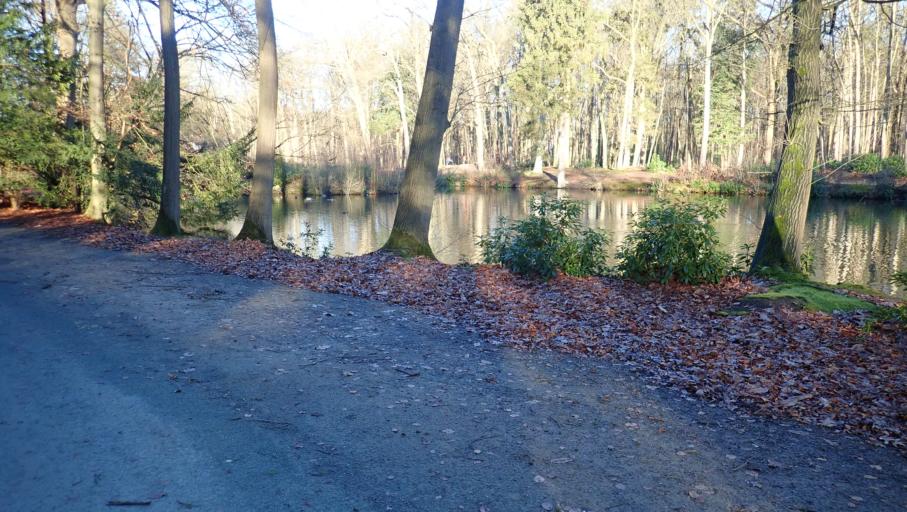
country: BE
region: Flanders
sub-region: Provincie Antwerpen
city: Schilde
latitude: 51.2497
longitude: 4.6278
